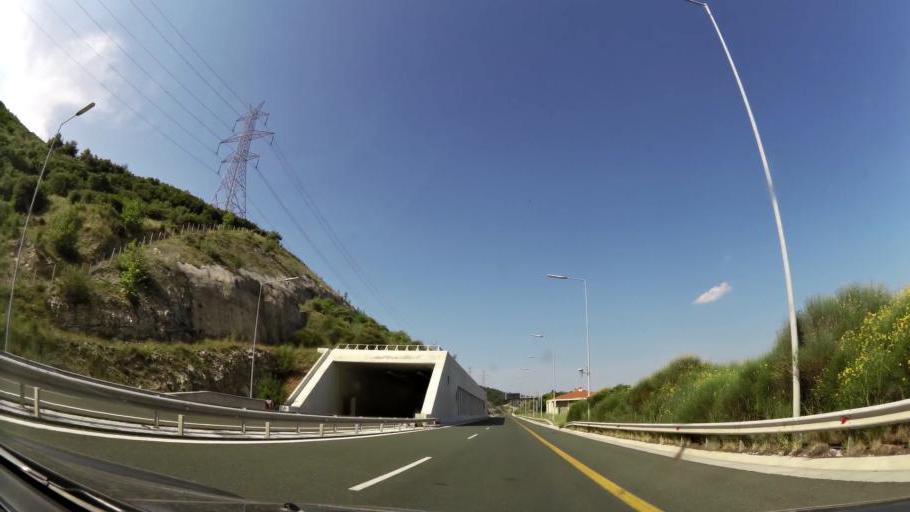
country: GR
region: Central Macedonia
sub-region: Nomos Imathias
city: Rizomata
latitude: 40.3944
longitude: 22.1593
